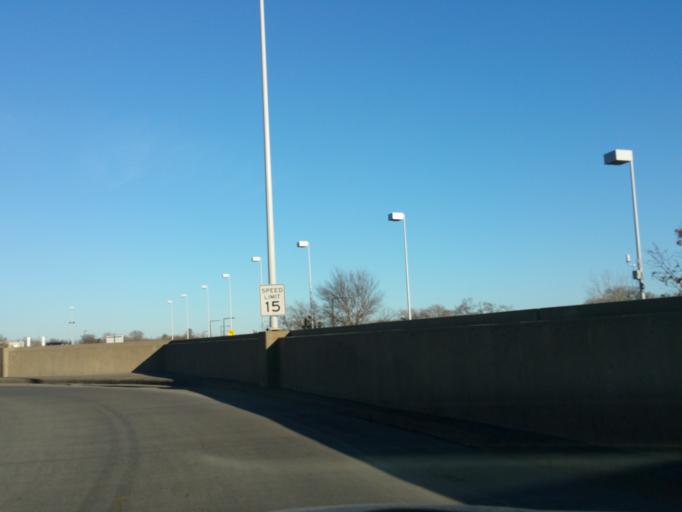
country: US
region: Minnesota
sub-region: Hennepin County
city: Richfield
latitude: 44.8528
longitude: -93.2401
